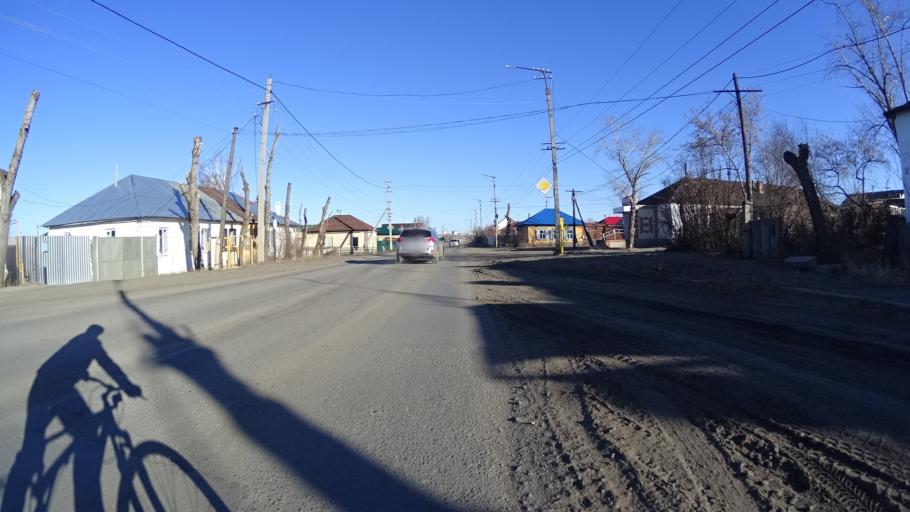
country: RU
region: Chelyabinsk
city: Troitsk
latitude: 54.0856
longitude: 61.5262
